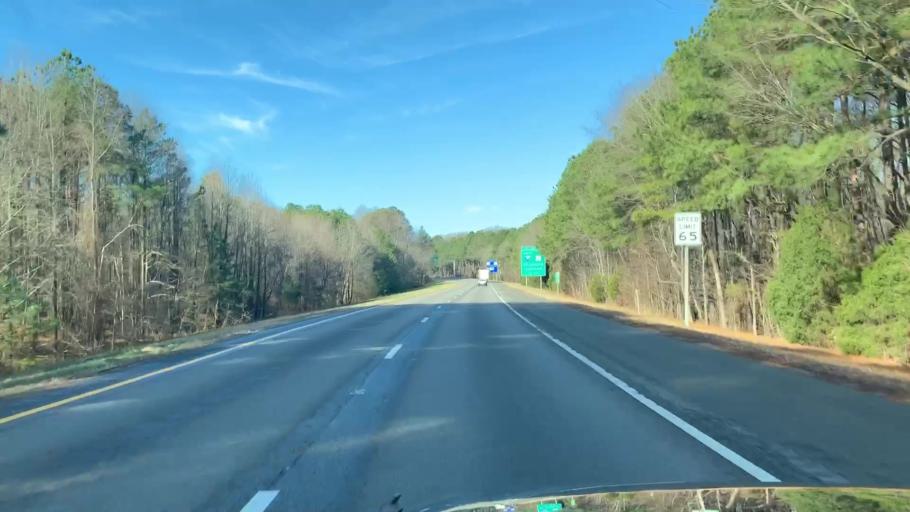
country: US
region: Virginia
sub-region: Henrico County
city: Chamberlayne
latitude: 37.6551
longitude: -77.4387
